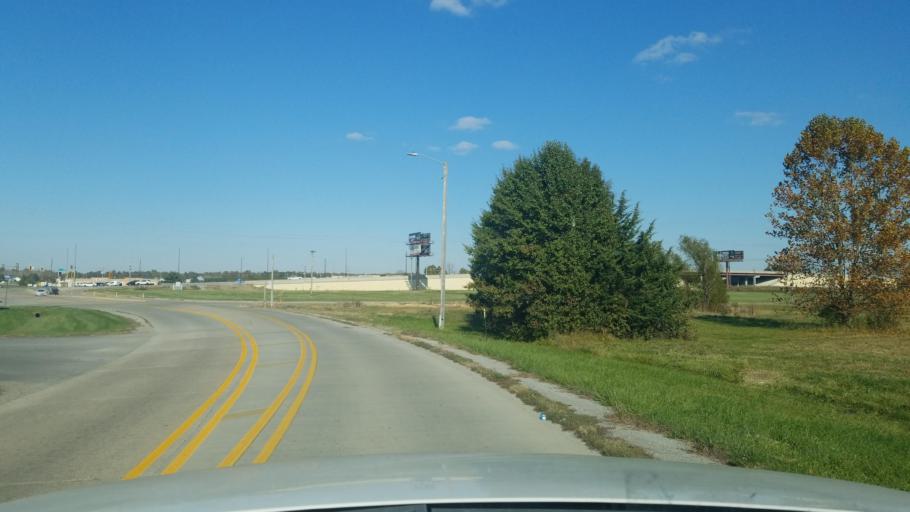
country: US
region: Illinois
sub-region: Williamson County
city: Marion
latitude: 37.7425
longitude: -88.9842
